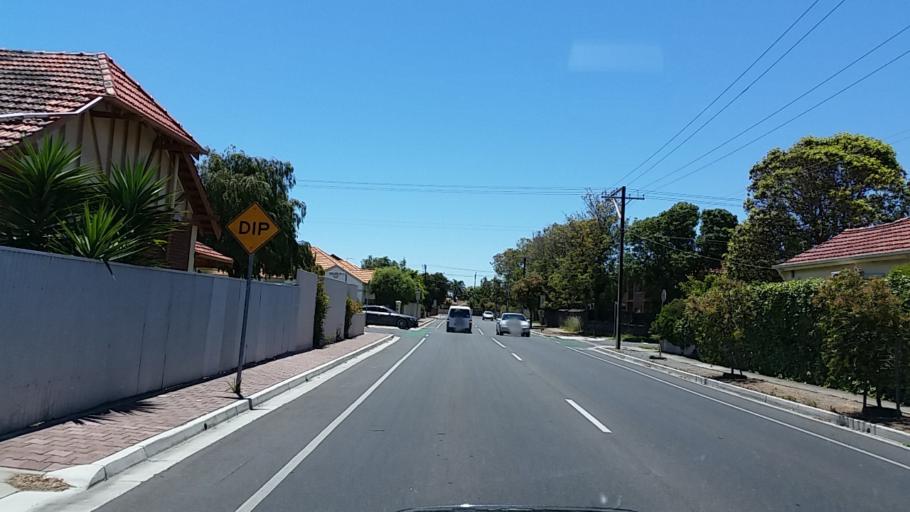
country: AU
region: South Australia
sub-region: Holdfast Bay
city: North Brighton
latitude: -34.9987
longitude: 138.5171
